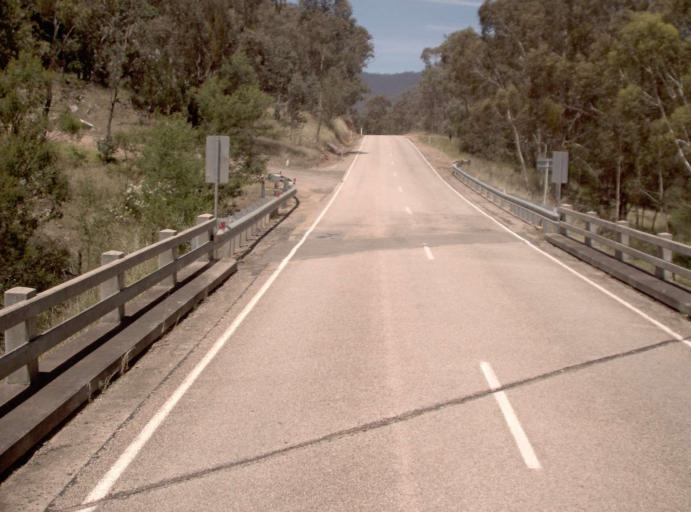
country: AU
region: Victoria
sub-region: East Gippsland
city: Bairnsdale
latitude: -37.3095
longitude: 147.7558
